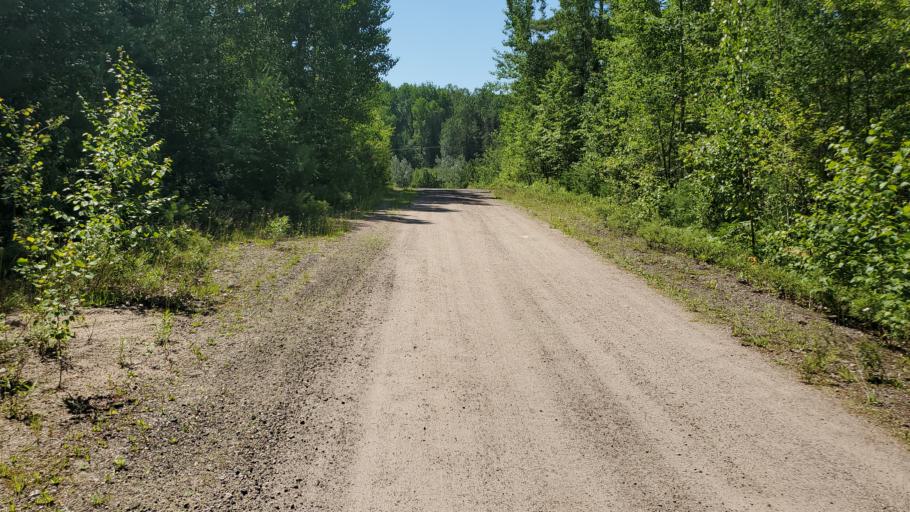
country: CA
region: Ontario
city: Mattawa
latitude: 46.2563
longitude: -78.2721
